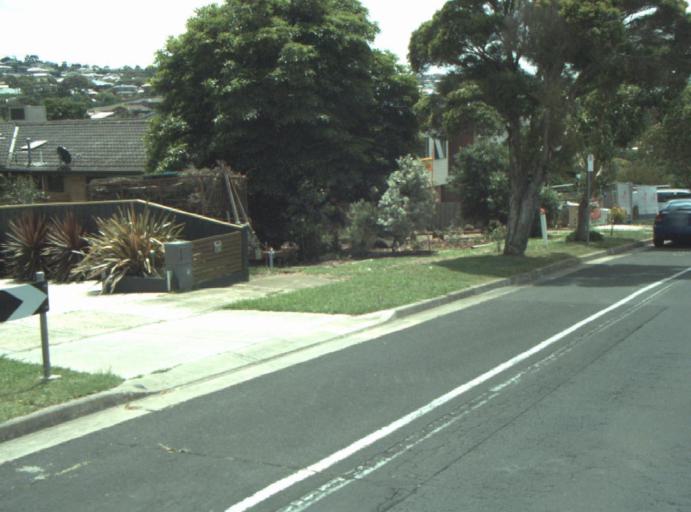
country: AU
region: Victoria
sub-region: Greater Geelong
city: Wandana Heights
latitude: -38.1802
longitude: 144.3114
